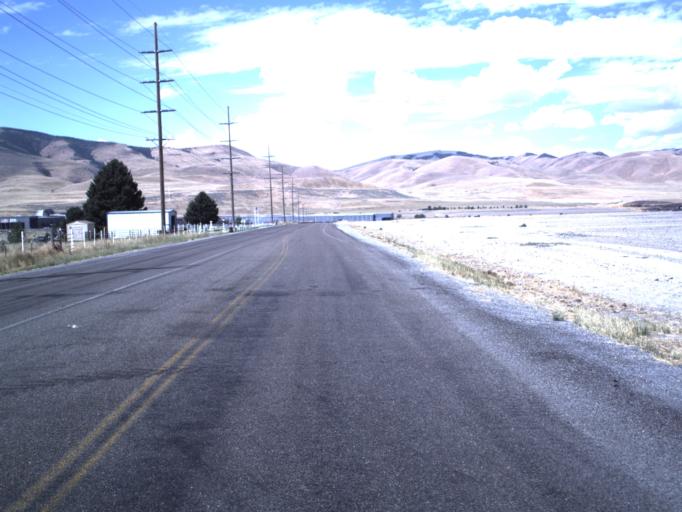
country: US
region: Utah
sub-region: Box Elder County
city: Garland
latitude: 41.8864
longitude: -112.1733
